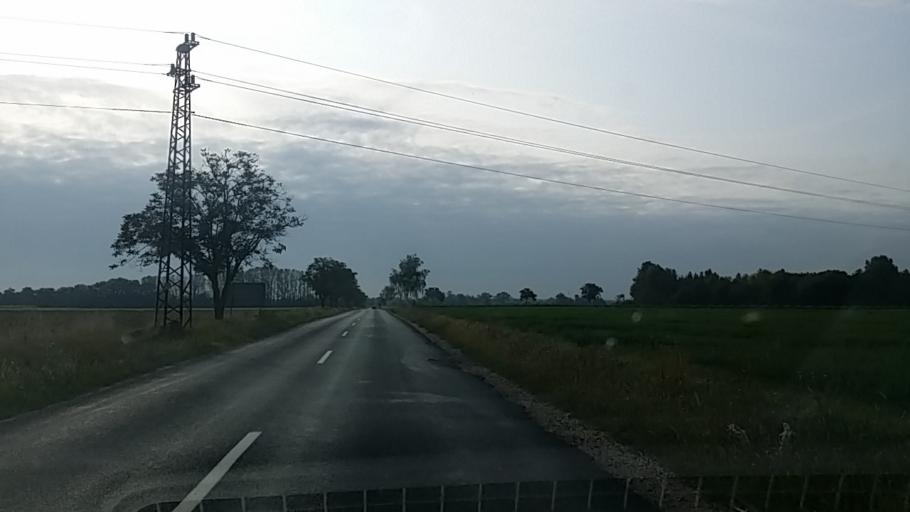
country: HU
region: Gyor-Moson-Sopron
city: Fertod
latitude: 47.6134
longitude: 16.8913
